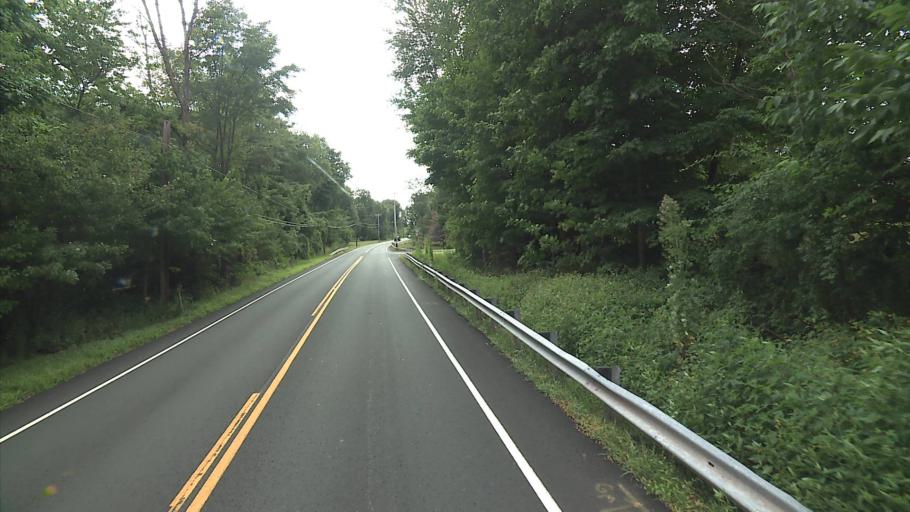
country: US
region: Connecticut
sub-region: Hartford County
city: West Hartford
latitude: 41.8122
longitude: -72.7601
